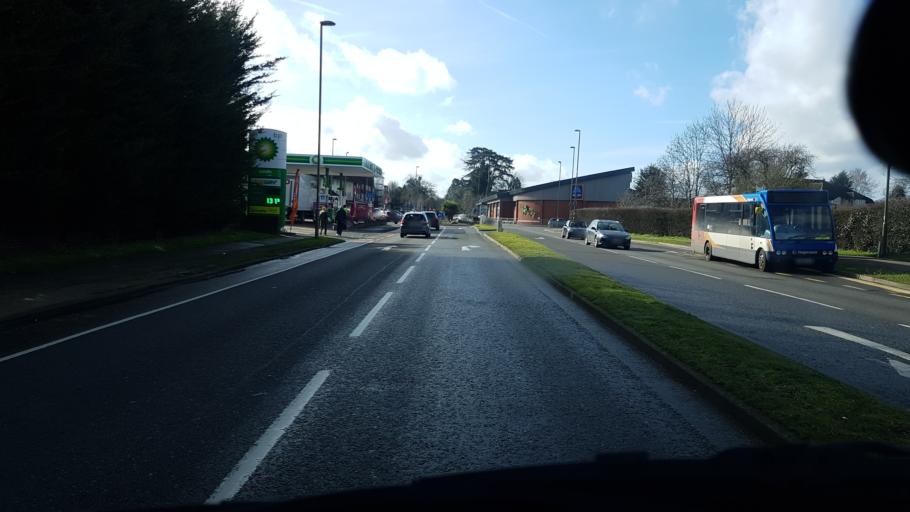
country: GB
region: England
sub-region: Surrey
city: Send
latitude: 51.2597
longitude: -0.5443
